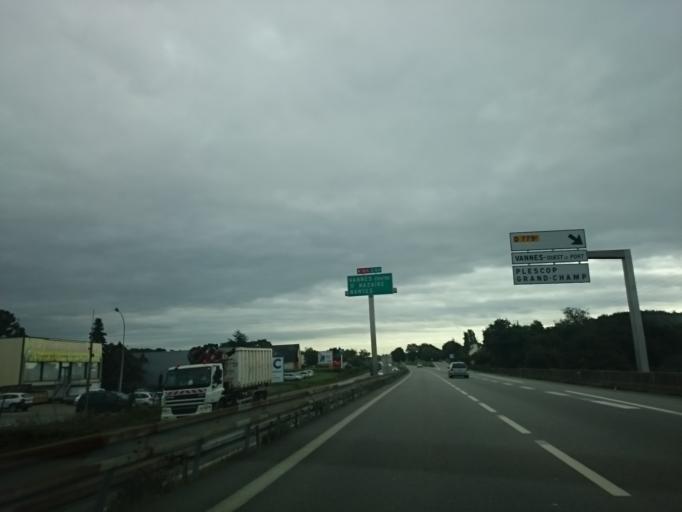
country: FR
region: Brittany
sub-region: Departement du Morbihan
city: Plescop
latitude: 47.6607
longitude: -2.8034
